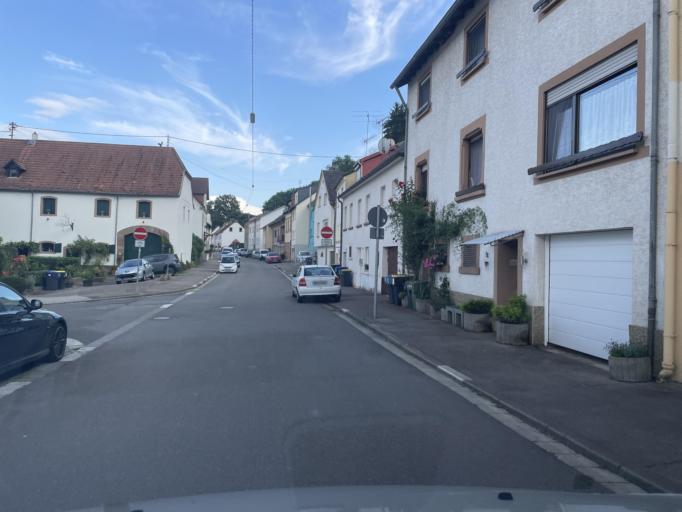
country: DE
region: Saarland
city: Kleinblittersdorf
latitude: 49.1975
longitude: 7.0639
